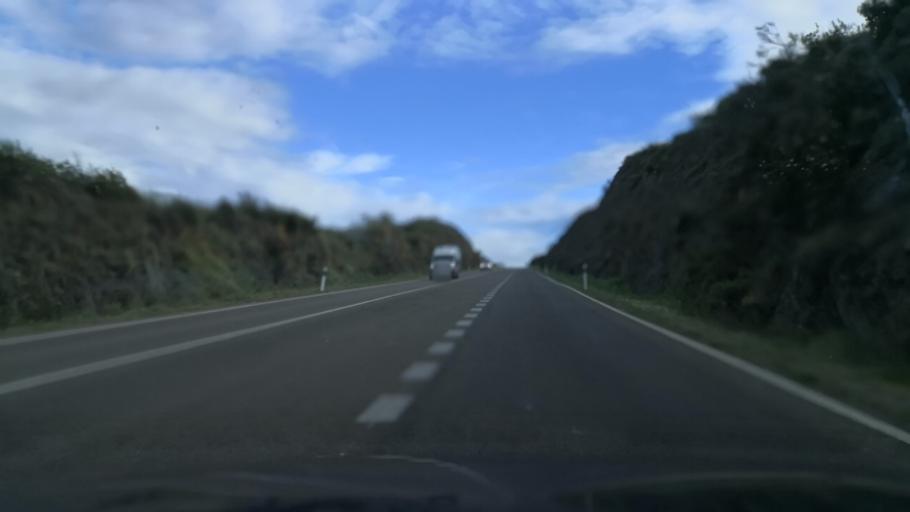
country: ES
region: Extremadura
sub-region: Provincia de Caceres
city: Coria
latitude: 39.9500
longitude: -6.5091
